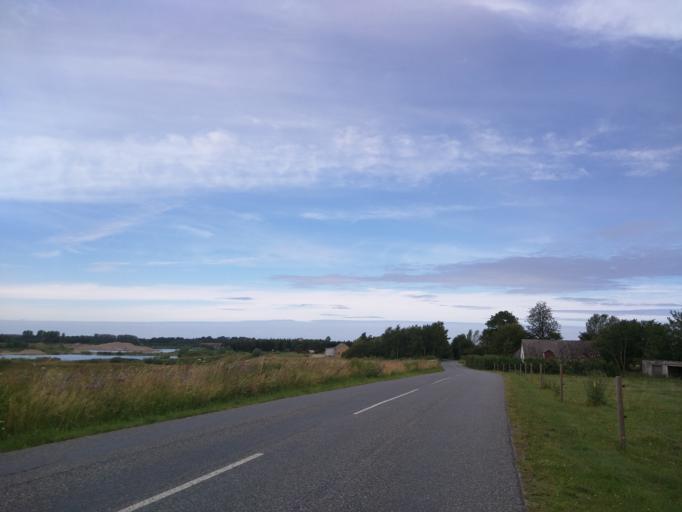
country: DK
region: Zealand
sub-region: Kalundborg Kommune
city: Svebolle
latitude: 55.6778
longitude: 11.3278
